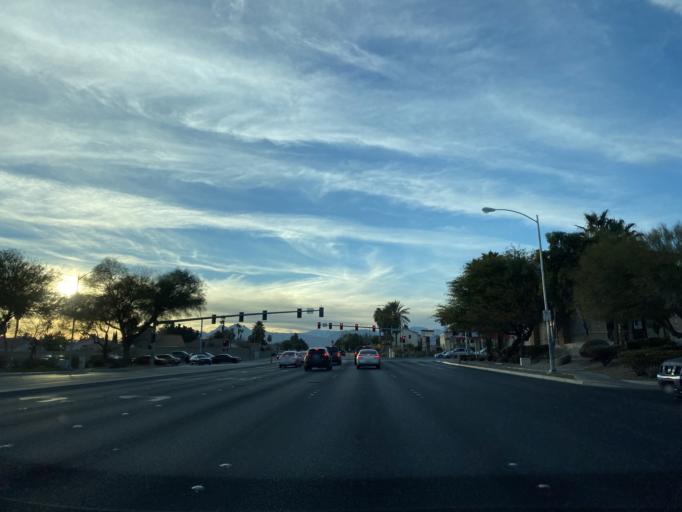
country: US
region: Nevada
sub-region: Clark County
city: North Las Vegas
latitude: 36.2617
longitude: -115.2061
